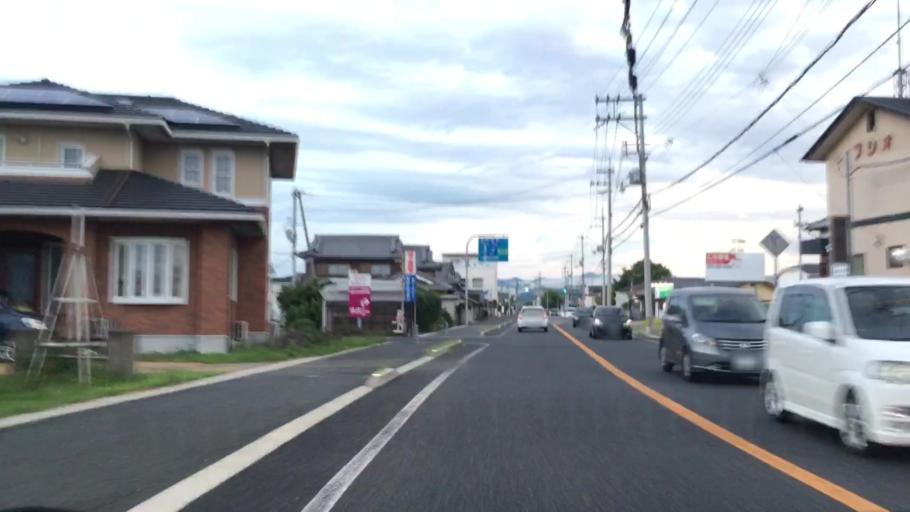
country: JP
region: Hyogo
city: Himeji
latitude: 34.9129
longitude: 134.7394
